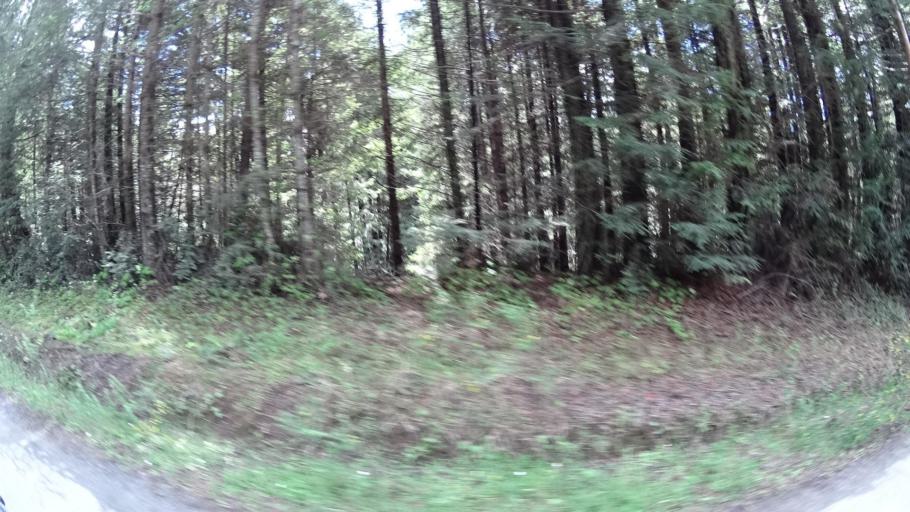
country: US
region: California
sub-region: Humboldt County
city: Blue Lake
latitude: 40.8401
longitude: -123.8949
